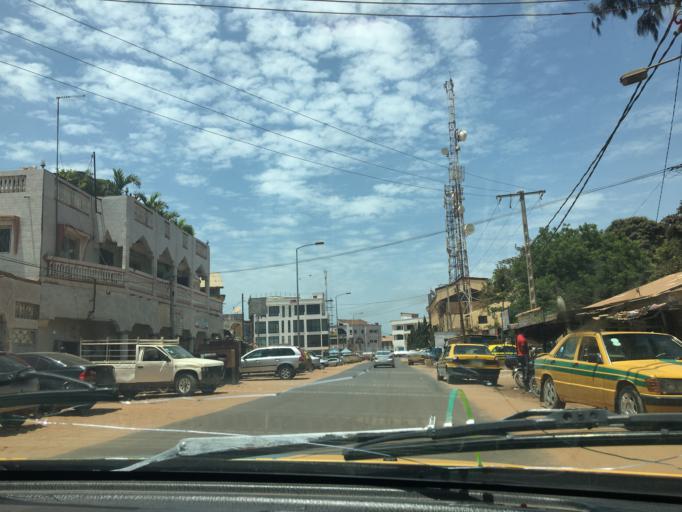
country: GM
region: Banjul
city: Bakau
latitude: 13.4531
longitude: -16.6827
